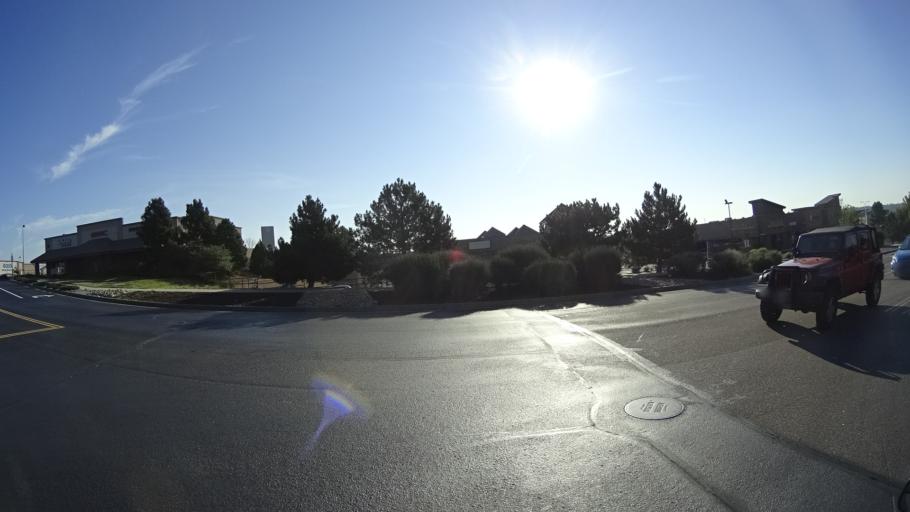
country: US
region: Colorado
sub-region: El Paso County
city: Cimarron Hills
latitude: 38.8867
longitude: -104.7178
